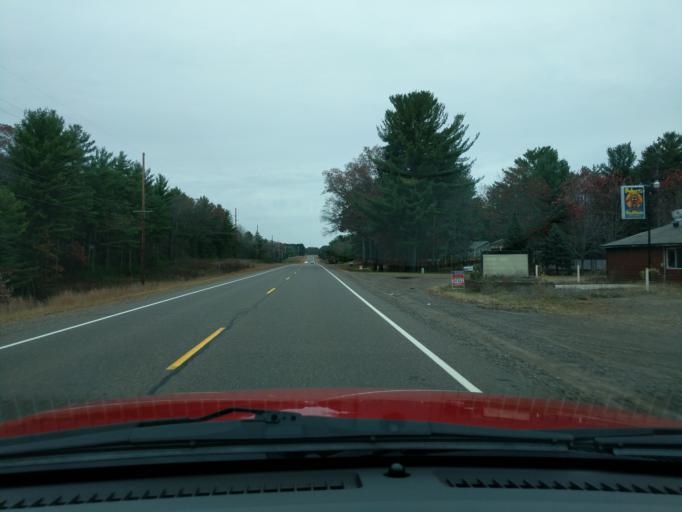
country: US
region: Wisconsin
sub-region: Burnett County
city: Siren
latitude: 45.8110
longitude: -92.2247
